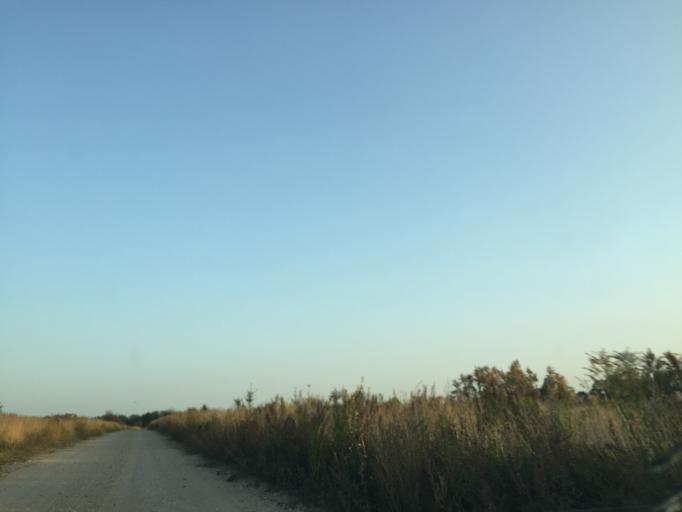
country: LV
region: Lielvarde
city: Lielvarde
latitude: 56.7605
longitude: 24.7833
